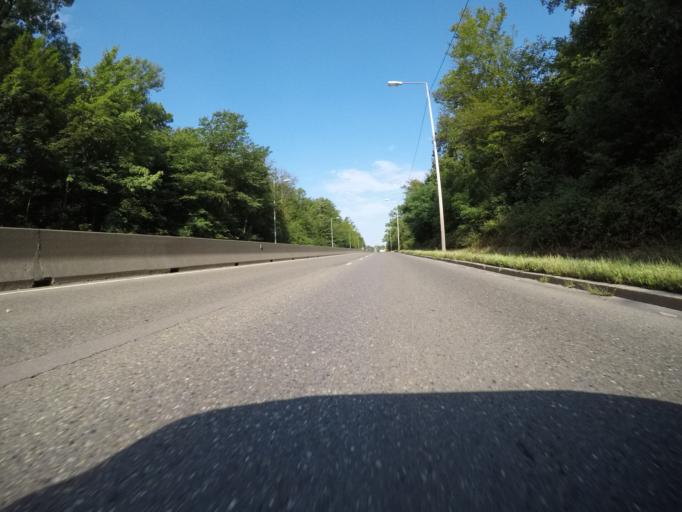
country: DE
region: Baden-Wuerttemberg
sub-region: Regierungsbezirk Stuttgart
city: Stuttgart
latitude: 48.7638
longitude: 9.1302
